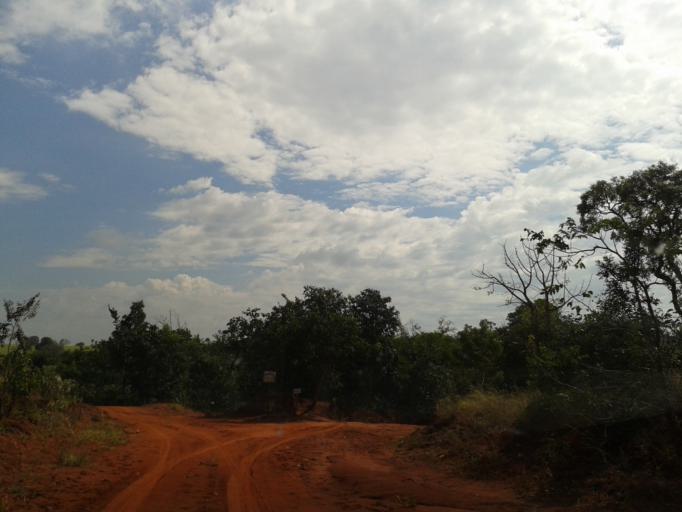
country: BR
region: Minas Gerais
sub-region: Campina Verde
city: Campina Verde
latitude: -19.3906
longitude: -49.6451
